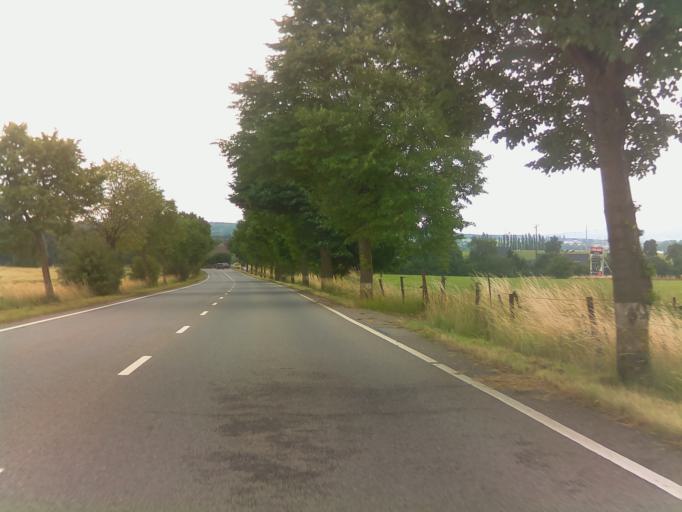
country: LU
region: Luxembourg
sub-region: Canton de Capellen
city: Dippach
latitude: 49.5798
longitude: 5.9856
